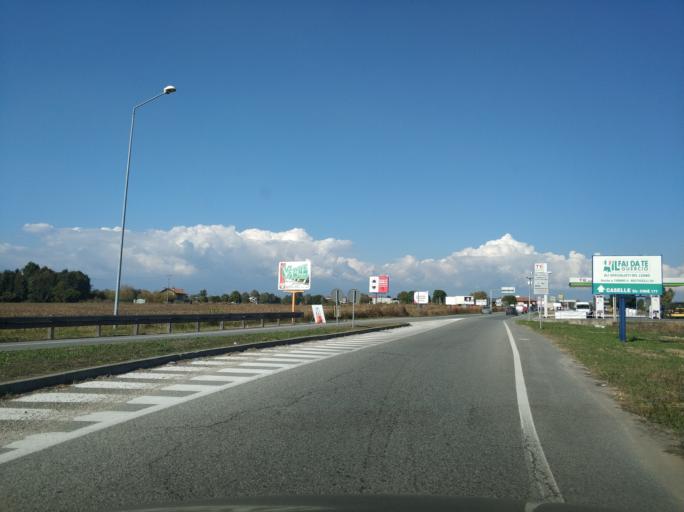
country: IT
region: Piedmont
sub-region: Provincia di Torino
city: Borgaro Torinese
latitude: 45.1598
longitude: 7.6549
